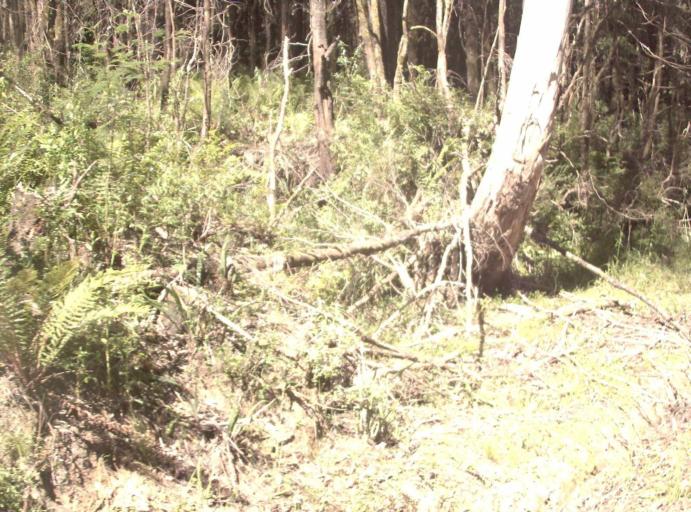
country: AU
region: Victoria
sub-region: Yarra Ranges
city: Millgrove
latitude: -37.5394
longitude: 145.8425
